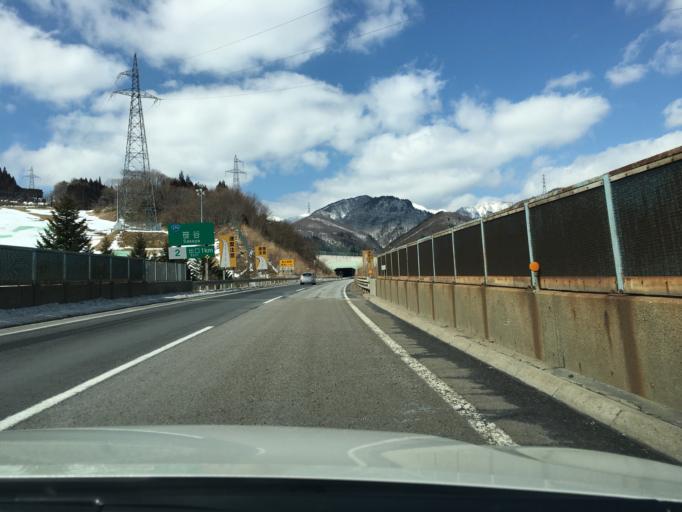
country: JP
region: Yamagata
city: Yamagata-shi
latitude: 38.2173
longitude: 140.5209
